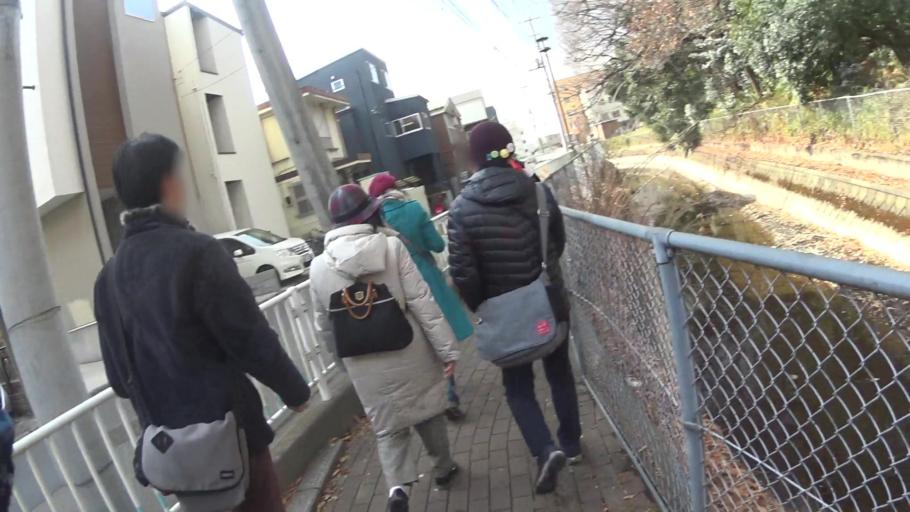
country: JP
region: Saitama
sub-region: Kawaguchi-shi
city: Hatogaya-honcho
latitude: 35.8570
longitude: 139.7035
